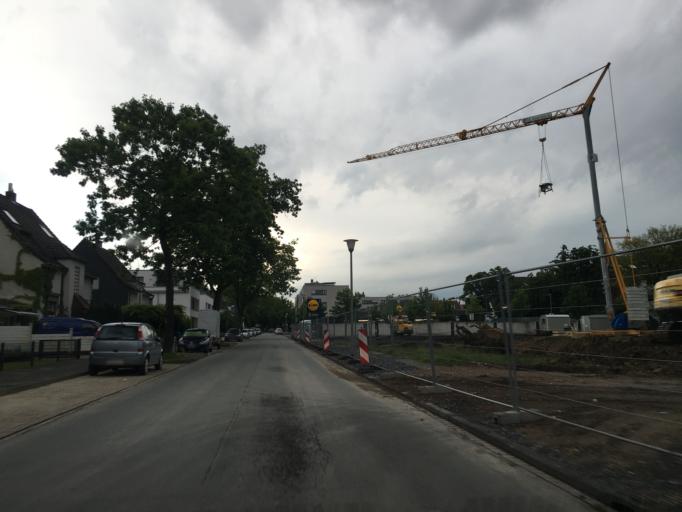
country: DE
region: North Rhine-Westphalia
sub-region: Regierungsbezirk Munster
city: Muenster
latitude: 51.9661
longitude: 7.5769
